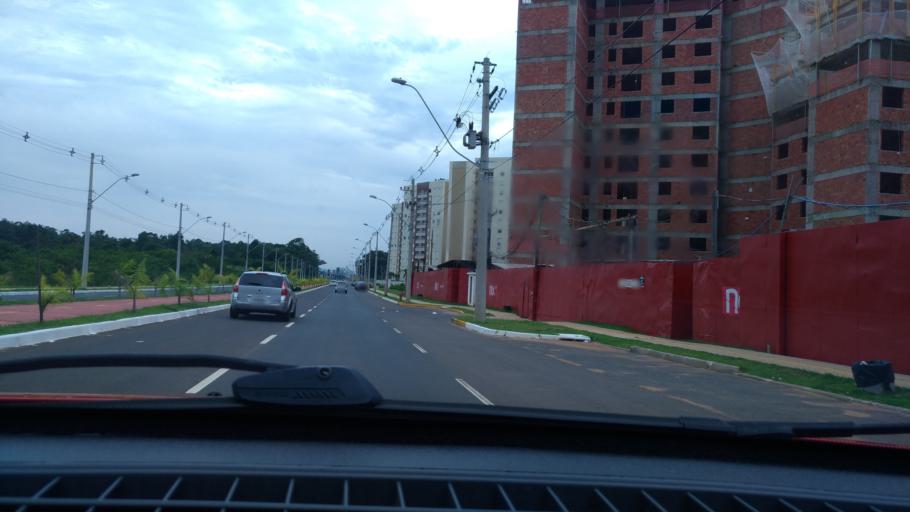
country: BR
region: Rio Grande do Sul
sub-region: Canoas
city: Canoas
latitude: -29.9069
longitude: -51.1650
